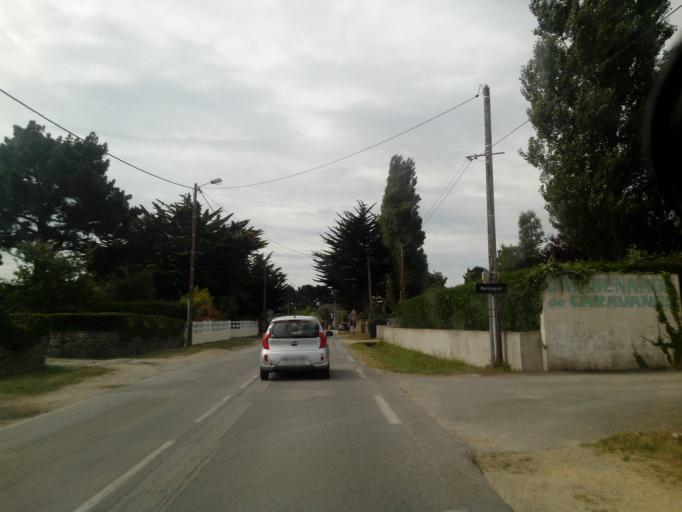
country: FR
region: Brittany
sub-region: Departement du Morbihan
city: Erdeven
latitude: 47.6315
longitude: -3.1582
